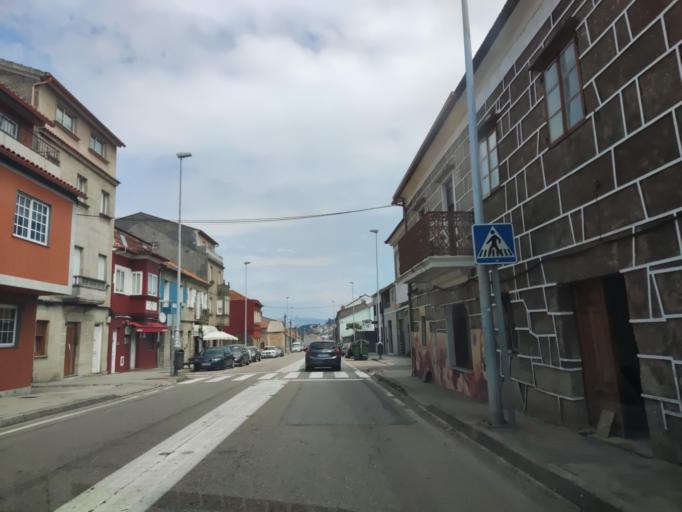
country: ES
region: Galicia
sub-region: Provincia de Pontevedra
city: Vigo
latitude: 42.2581
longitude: -8.6807
